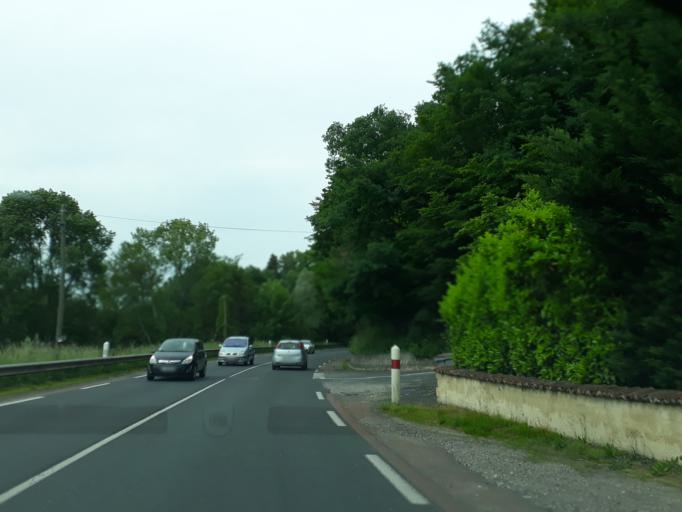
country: FR
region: Limousin
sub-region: Departement de la Correze
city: Saint-Pantaleon-de-Larche
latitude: 45.1337
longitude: 1.4445
